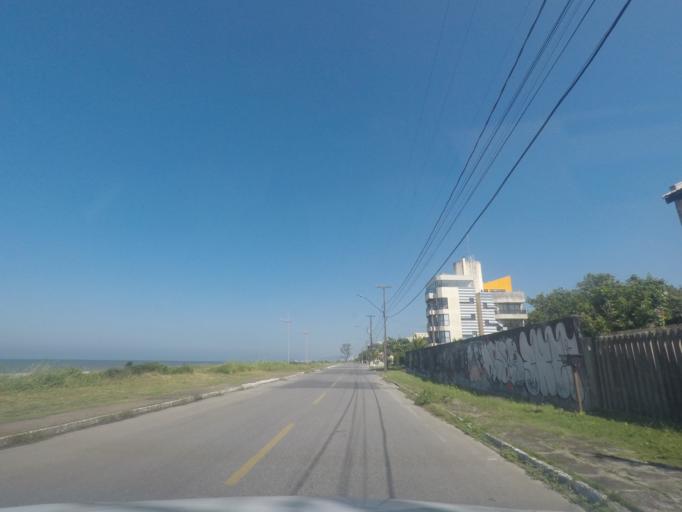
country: BR
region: Parana
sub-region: Pontal Do Parana
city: Pontal do Parana
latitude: -25.7528
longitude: -48.5019
